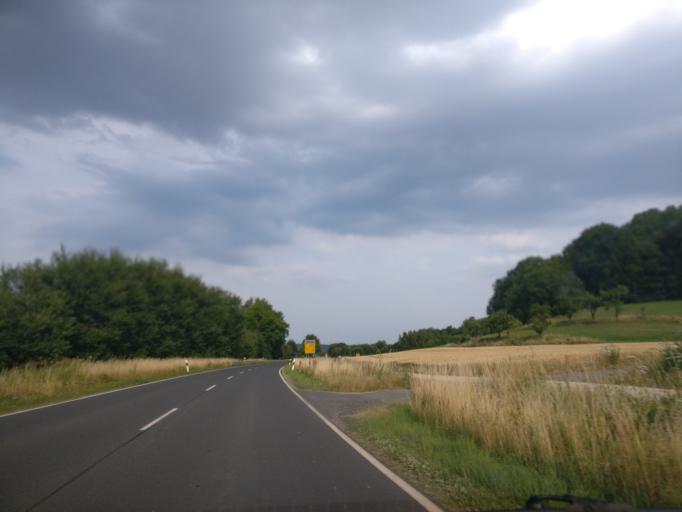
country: DE
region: Lower Saxony
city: Hardegsen
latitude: 51.5859
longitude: 9.8548
